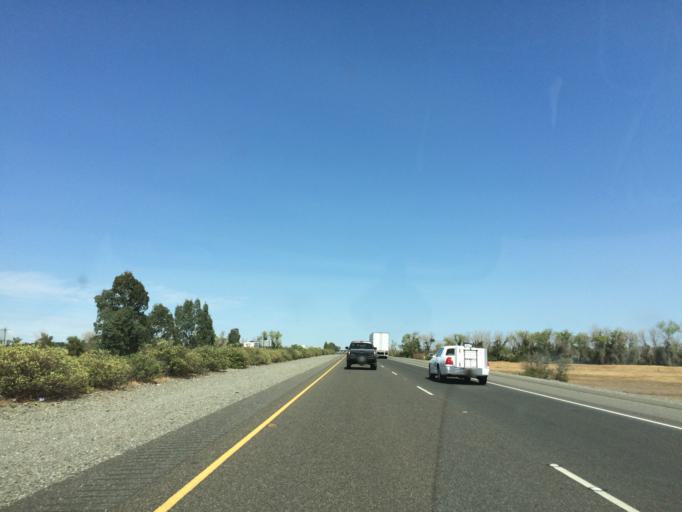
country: US
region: California
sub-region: Glenn County
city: Orland
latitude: 39.7667
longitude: -122.2050
